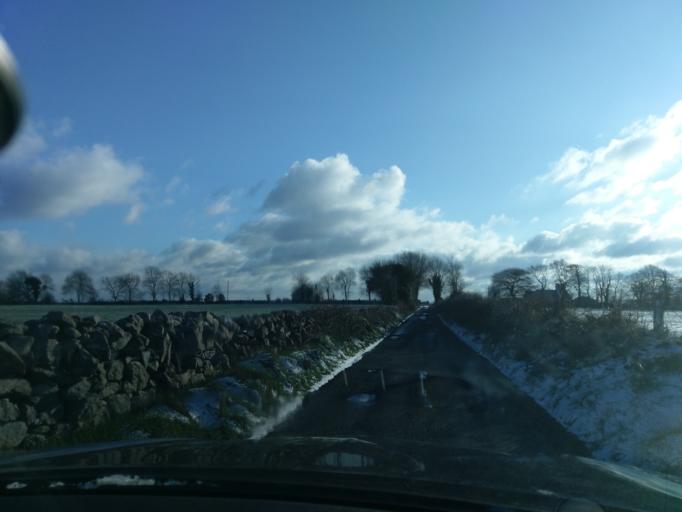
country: IE
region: Connaught
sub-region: County Galway
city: Gort
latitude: 53.1731
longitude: -8.7940
